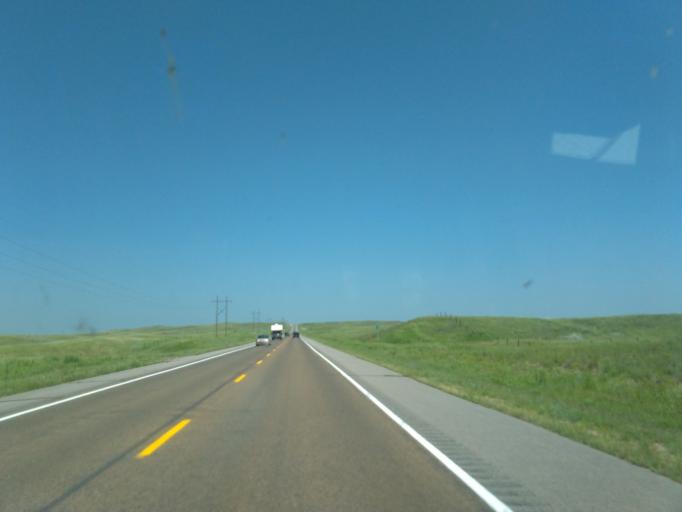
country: US
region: Nebraska
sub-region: Lincoln County
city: North Platte
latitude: 40.8597
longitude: -100.7541
